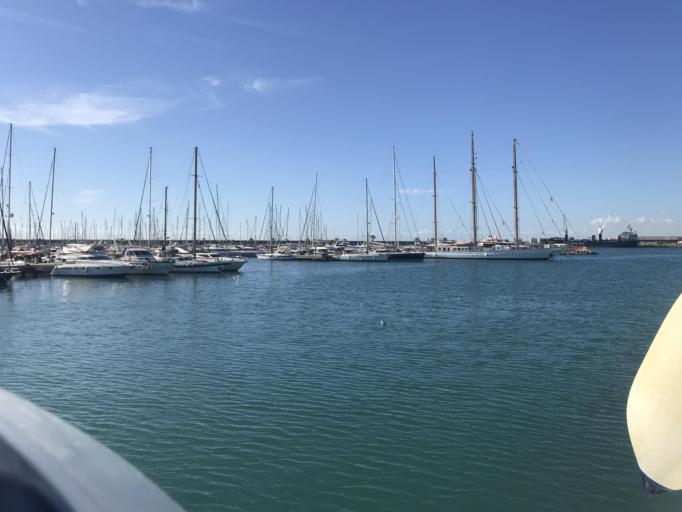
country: ES
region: Valencia
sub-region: Provincia de Alicante
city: Torrevieja
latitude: 37.9730
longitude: -0.6831
